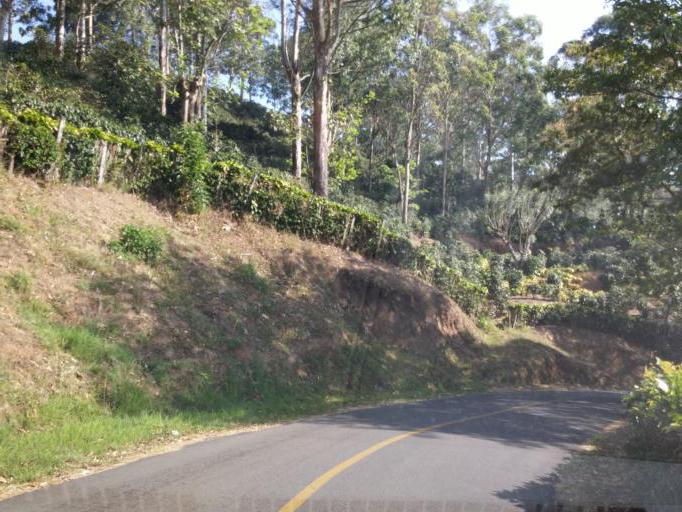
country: CR
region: Alajuela
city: Sabanilla
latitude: 10.0793
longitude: -84.1851
